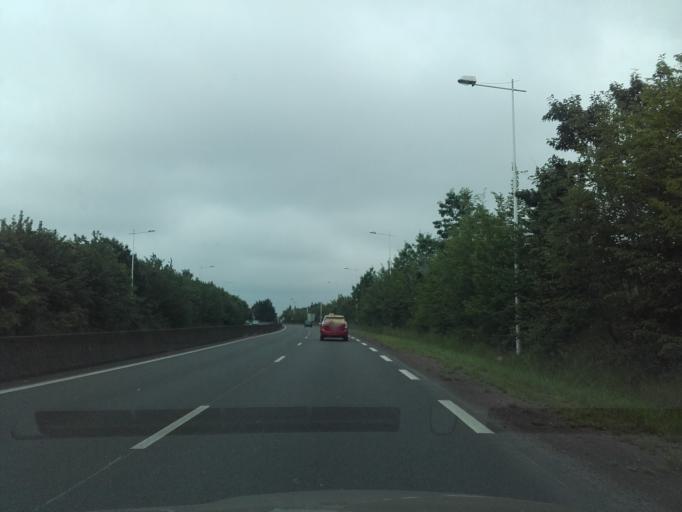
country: FR
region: Centre
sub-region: Departement d'Indre-et-Loire
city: Parcay-Meslay
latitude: 47.4225
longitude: 0.7151
